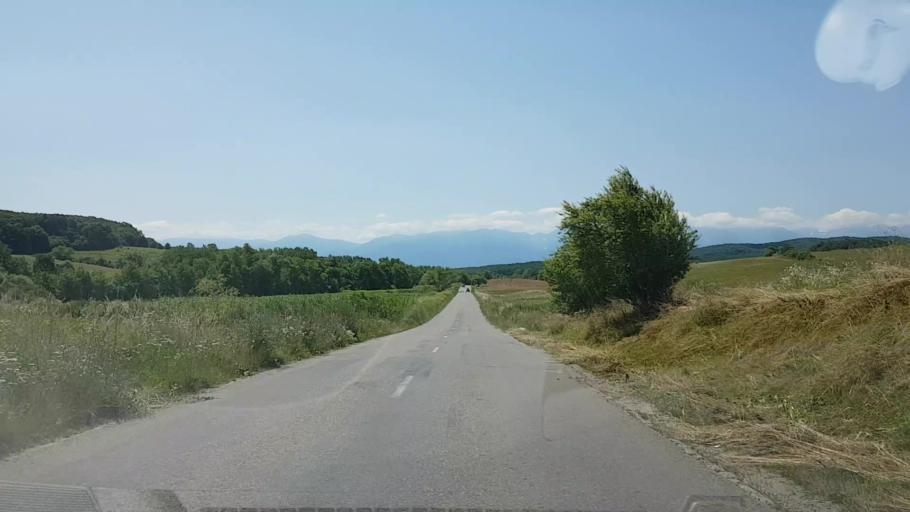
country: RO
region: Brasov
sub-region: Comuna Cincu
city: Cincu
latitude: 45.9028
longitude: 24.8118
